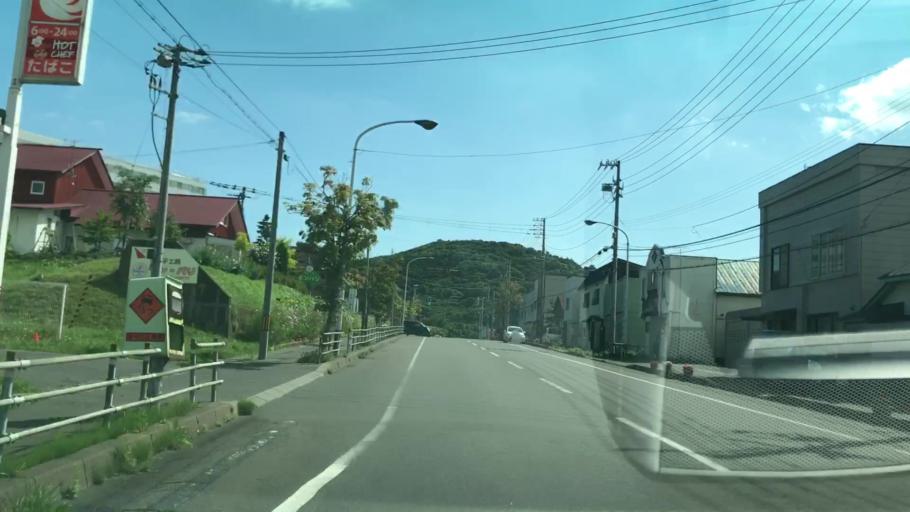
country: JP
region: Hokkaido
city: Muroran
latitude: 42.3232
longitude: 140.9967
